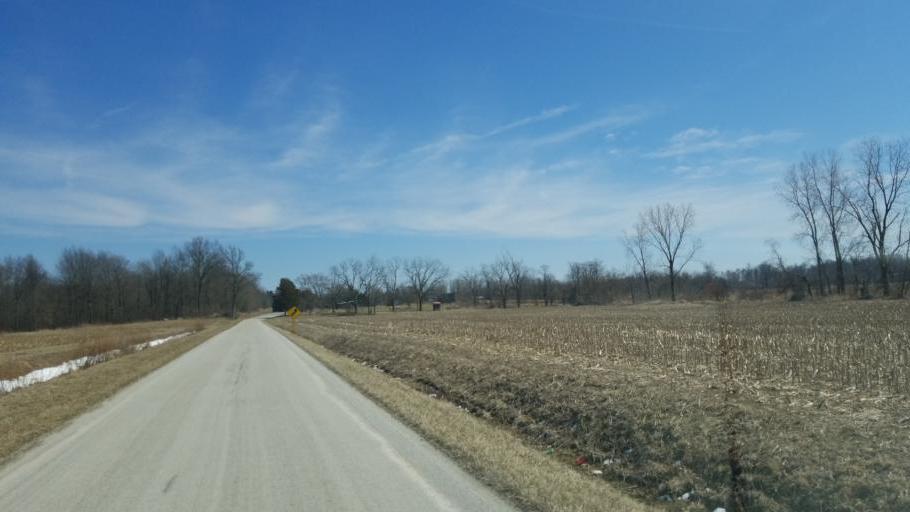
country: US
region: Ohio
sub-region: Crawford County
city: Galion
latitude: 40.6616
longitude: -82.8058
